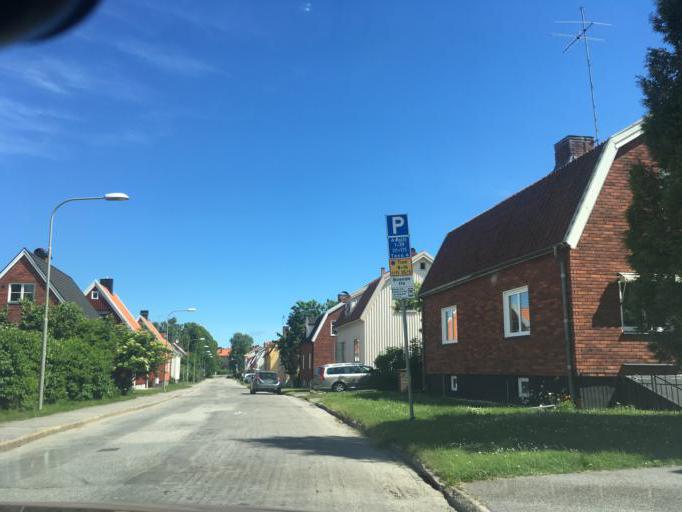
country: SE
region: Stockholm
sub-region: Nacka Kommun
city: Nacka
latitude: 59.2770
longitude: 18.1121
